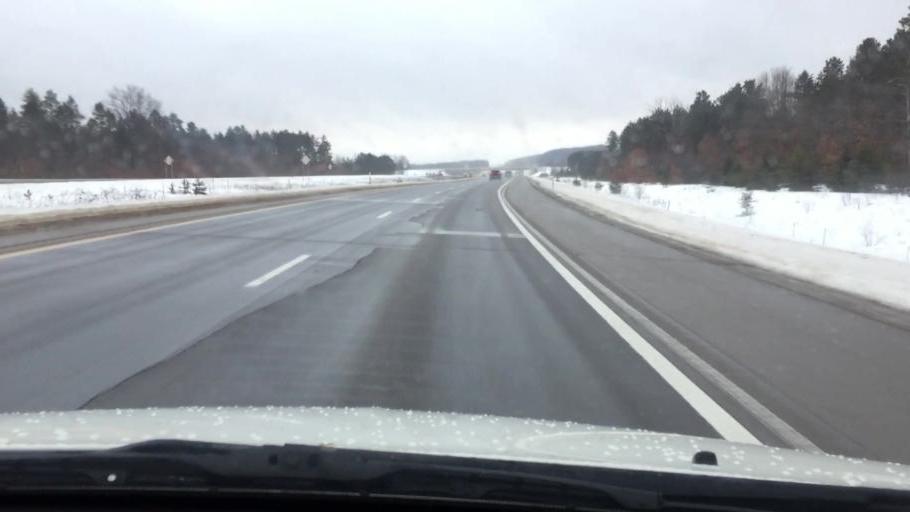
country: US
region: Michigan
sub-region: Wexford County
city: Manton
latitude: 44.4618
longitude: -85.3959
